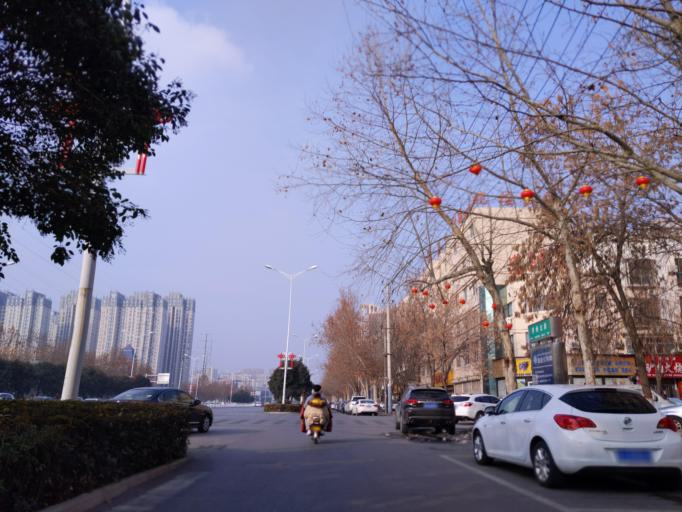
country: CN
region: Henan Sheng
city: Puyang
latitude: 35.7827
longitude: 115.0208
